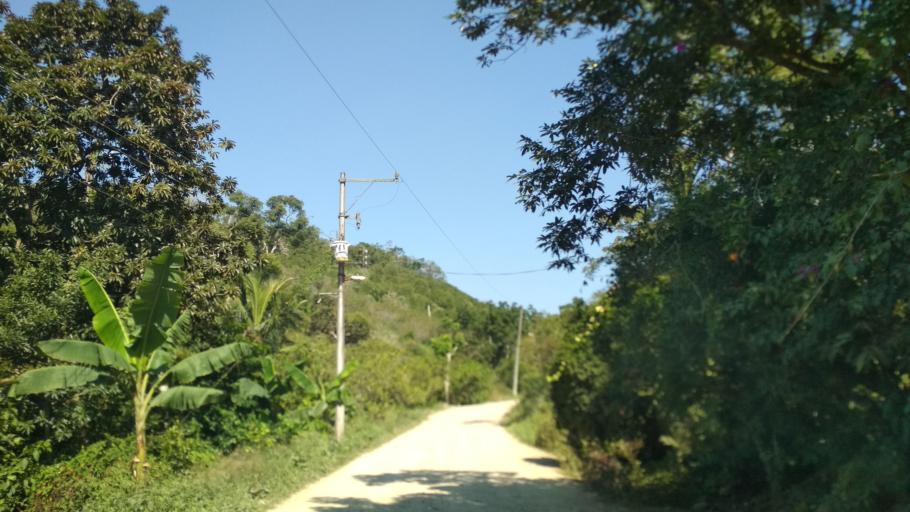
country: MX
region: Veracruz
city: Gutierrez Zamora
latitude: 20.4679
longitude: -97.1541
